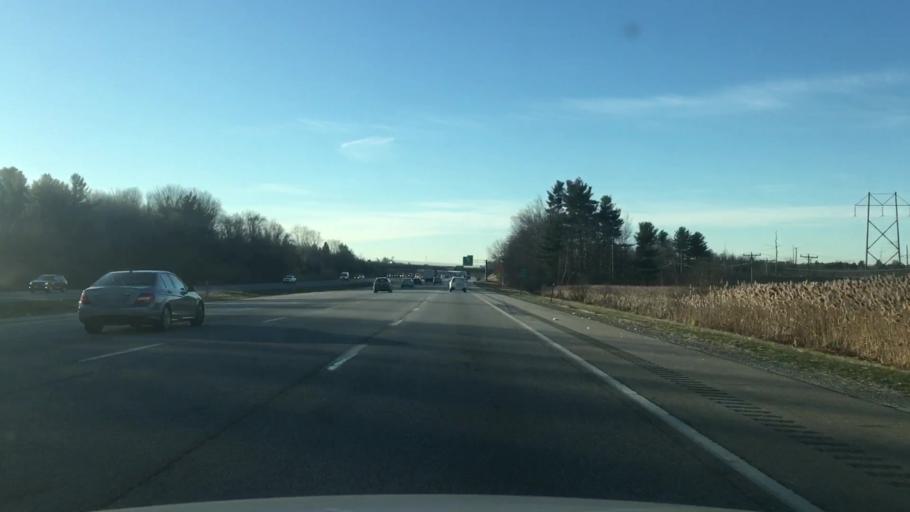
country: US
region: New Hampshire
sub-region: Rockingham County
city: North Hampton
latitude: 42.9803
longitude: -70.8530
